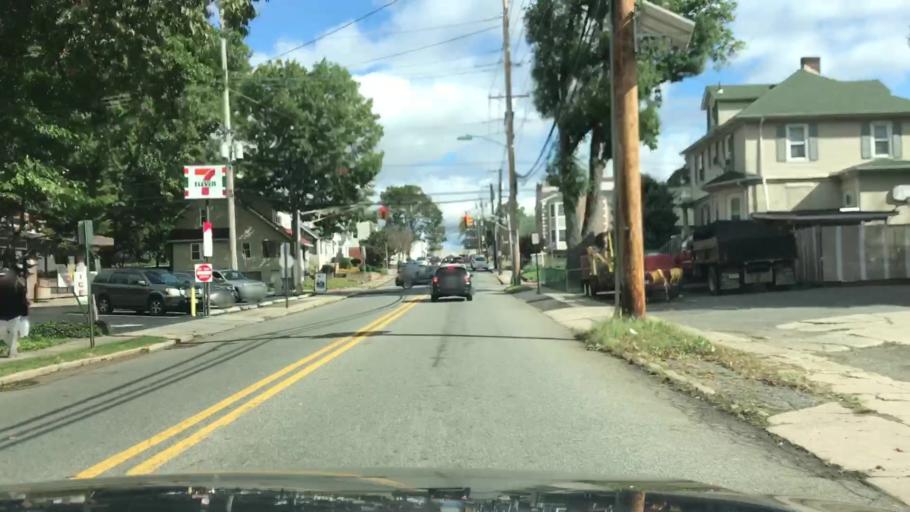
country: US
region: New Jersey
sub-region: Bergen County
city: Dumont
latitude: 40.9402
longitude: -73.9998
